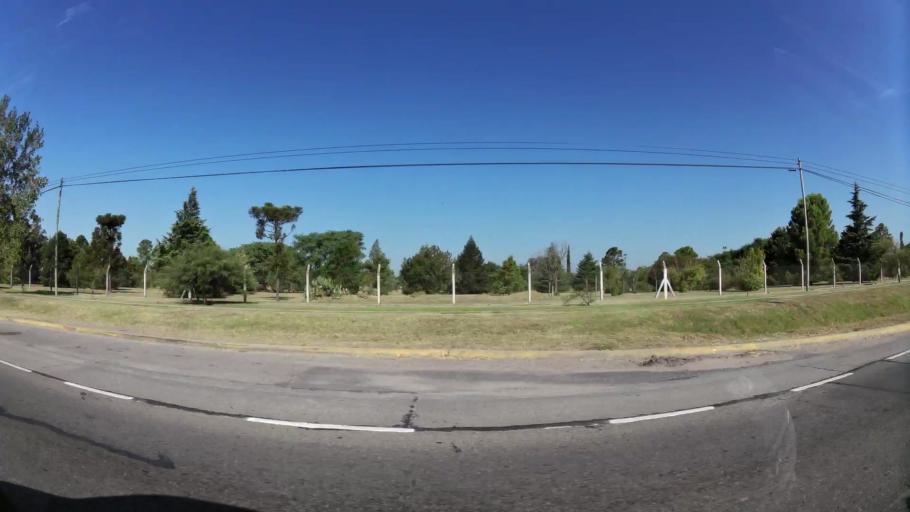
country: AR
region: Cordoba
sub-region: Departamento de Capital
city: Cordoba
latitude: -31.4849
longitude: -64.2451
